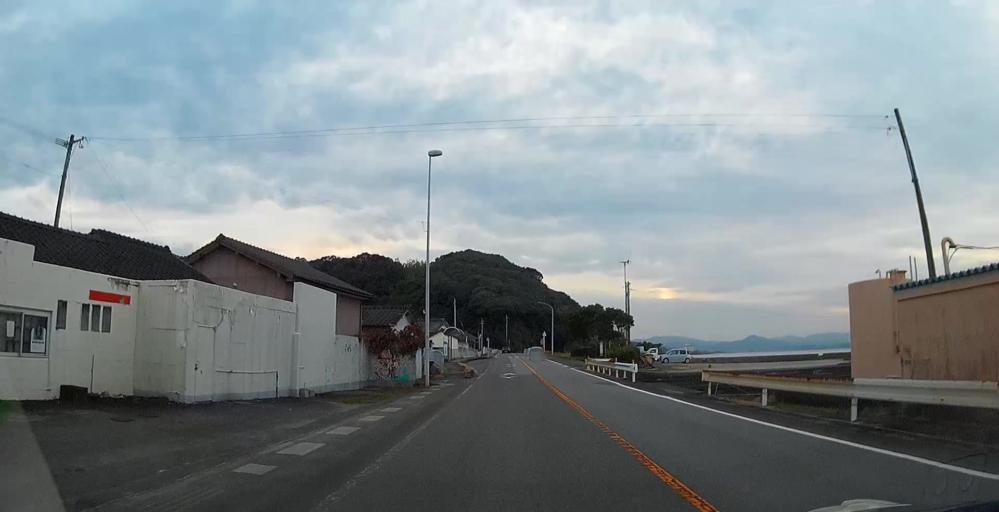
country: JP
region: Kumamoto
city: Hondo
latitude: 32.4917
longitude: 130.2937
